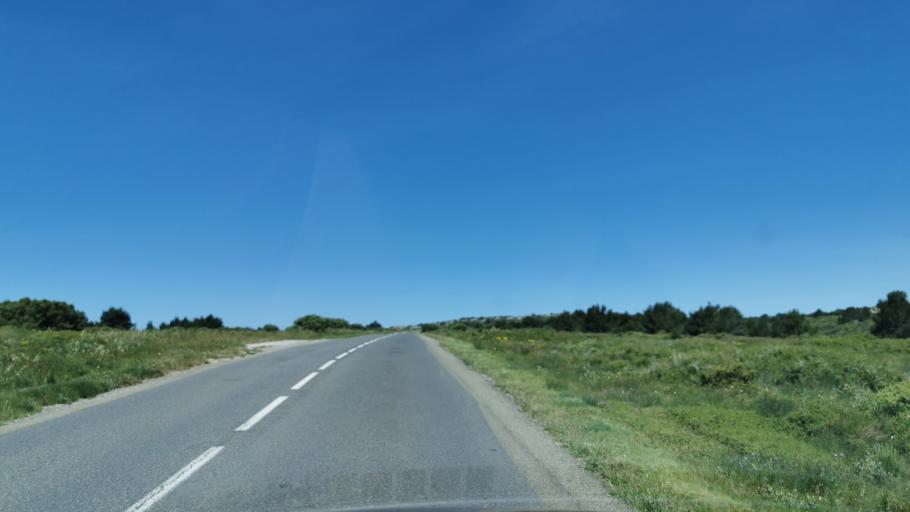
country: FR
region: Languedoc-Roussillon
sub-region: Departement de l'Aude
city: Armissan
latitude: 43.1605
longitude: 3.1410
